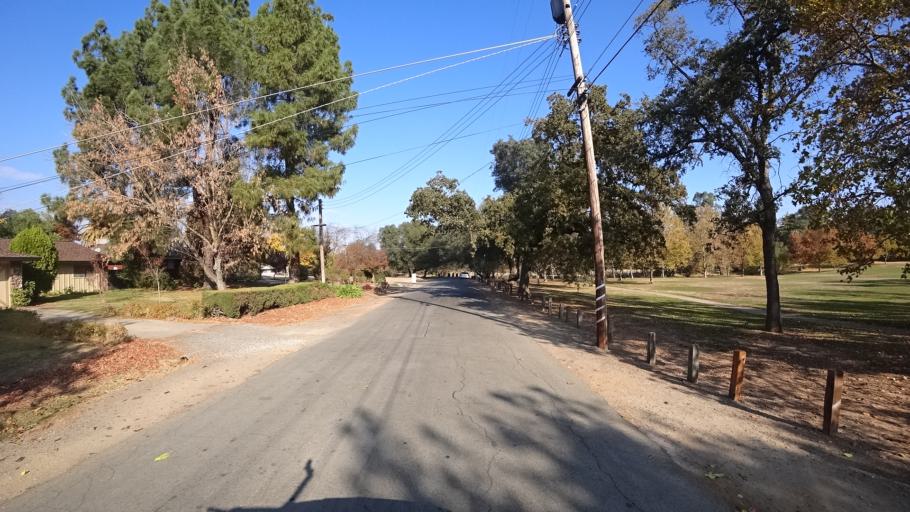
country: US
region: California
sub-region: Sacramento County
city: Citrus Heights
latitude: 38.7141
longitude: -121.2694
